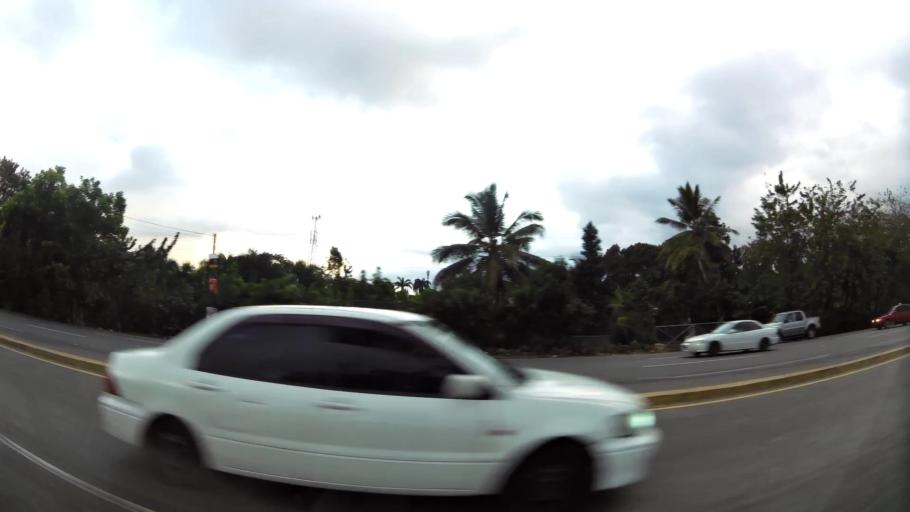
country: DO
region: Santo Domingo
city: Santo Domingo Oeste
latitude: 18.5643
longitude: -70.0757
